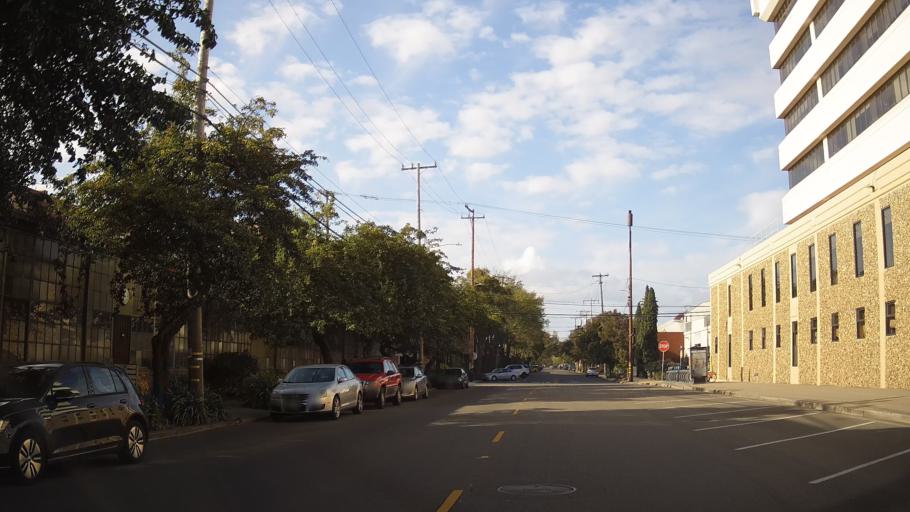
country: US
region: California
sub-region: Alameda County
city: Berkeley
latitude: 37.8583
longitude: -122.2911
